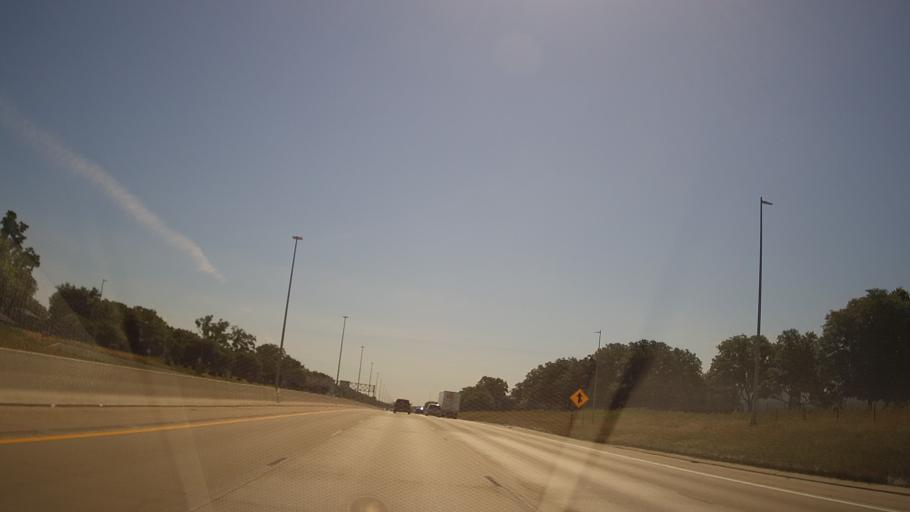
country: US
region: Michigan
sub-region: Wayne County
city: Livonia
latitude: 42.3819
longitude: -83.3997
